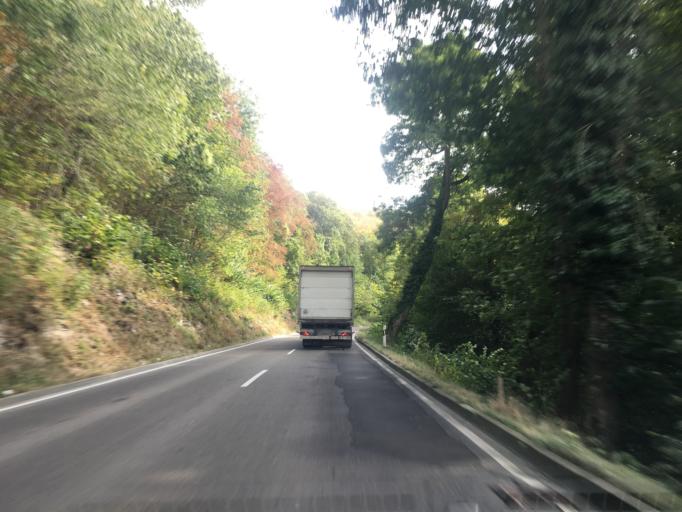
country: DE
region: Baden-Wuerttemberg
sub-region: Tuebingen Region
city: Pfullingen
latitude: 48.4197
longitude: 9.1806
